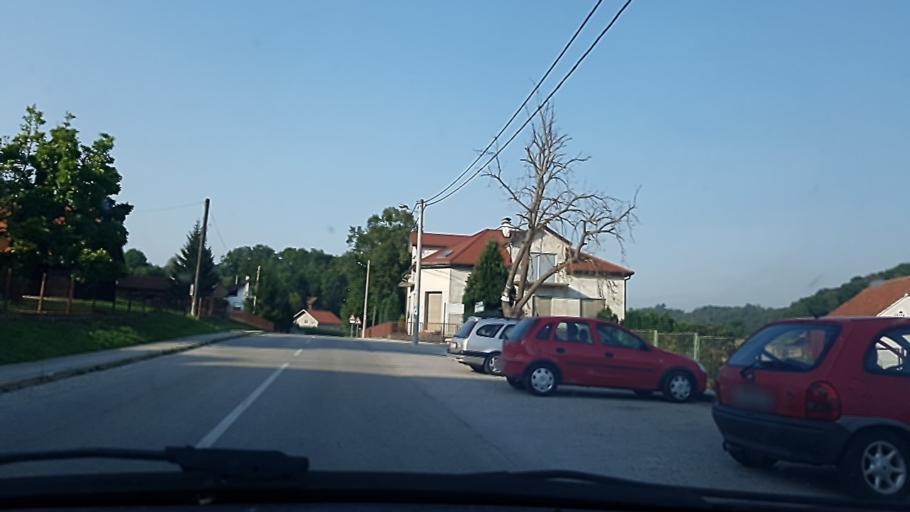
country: HR
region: Zagrebacka
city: Jakovlje
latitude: 45.9606
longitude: 15.8204
